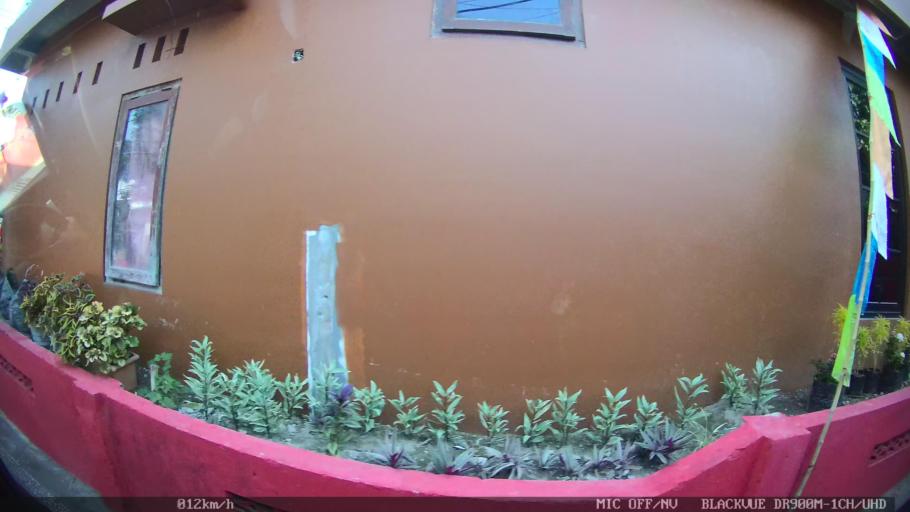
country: ID
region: Daerah Istimewa Yogyakarta
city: Sewon
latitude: -7.8359
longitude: 110.3987
